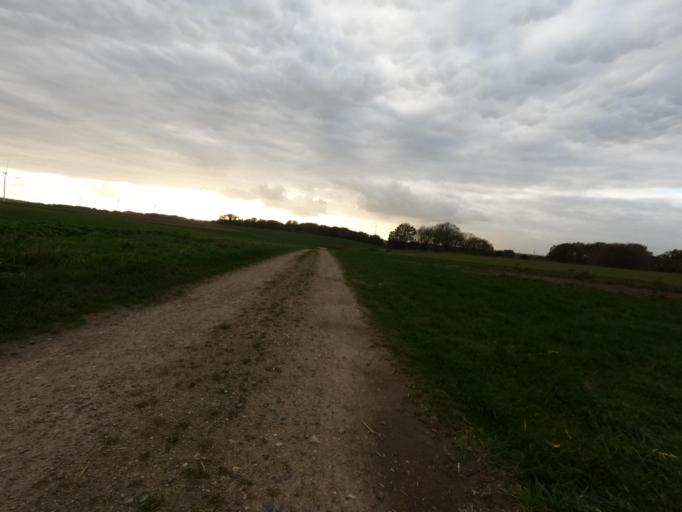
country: DE
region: North Rhine-Westphalia
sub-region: Regierungsbezirk Koln
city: Heinsberg
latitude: 51.0295
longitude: 6.1527
